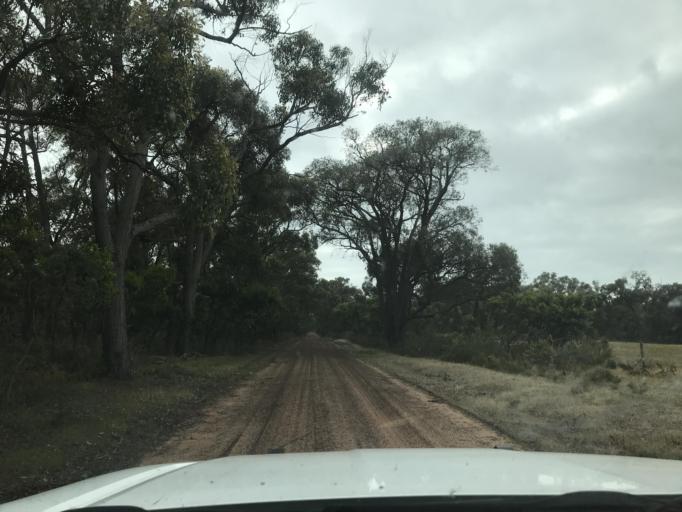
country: AU
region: South Australia
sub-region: Wattle Range
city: Penola
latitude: -37.1173
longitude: 141.1209
